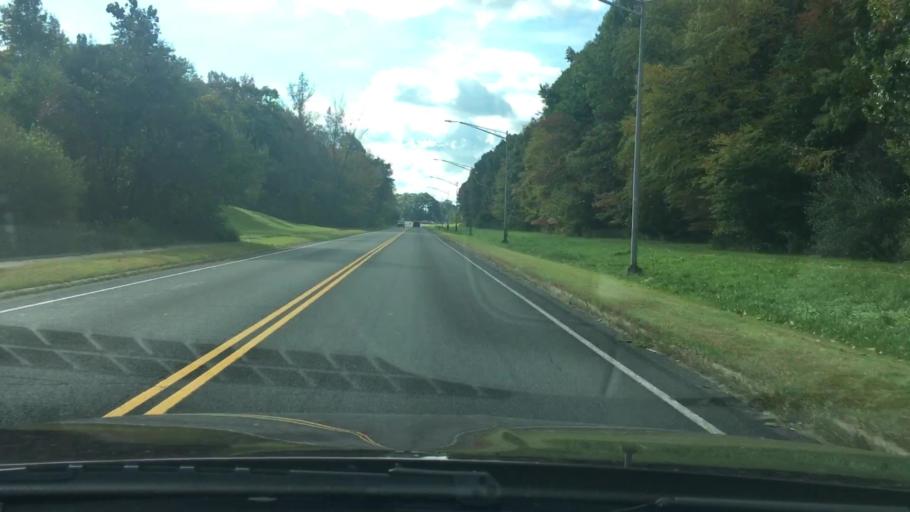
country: US
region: Connecticut
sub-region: New Haven County
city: Meriden
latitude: 41.4996
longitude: -72.7642
